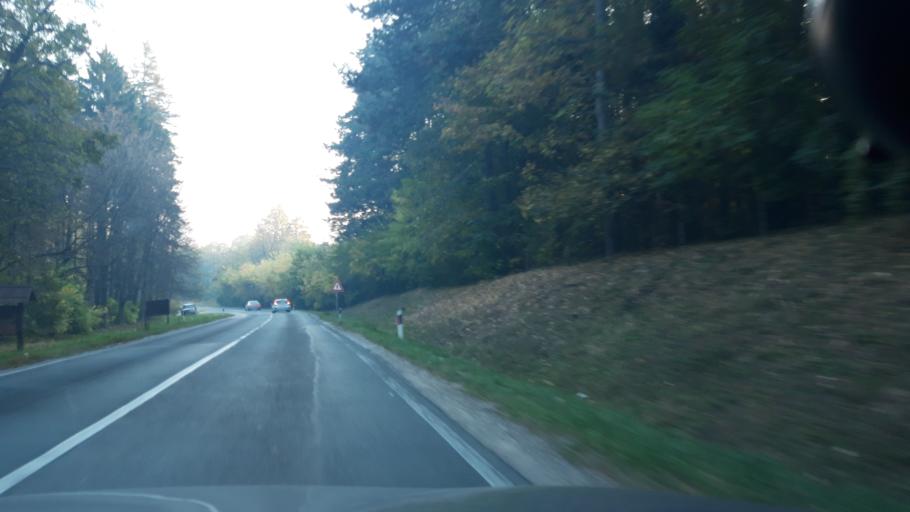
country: RS
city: Vrdnik
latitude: 45.1482
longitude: 19.8292
